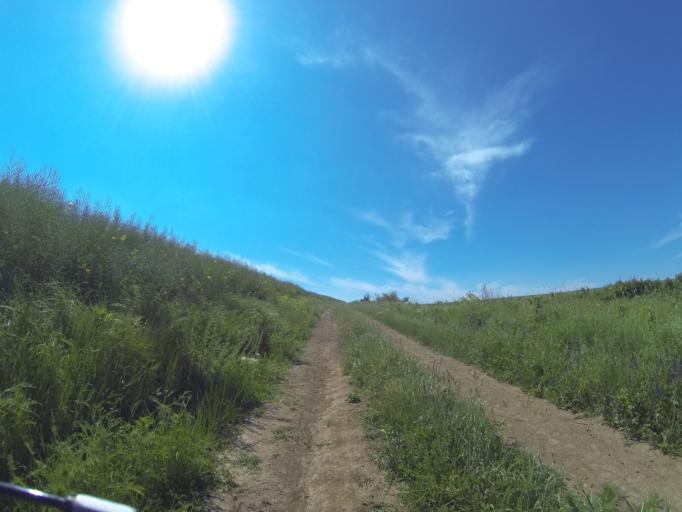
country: RO
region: Dolj
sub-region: Comuna Leu
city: Leu
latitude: 44.2539
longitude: 24.0144
